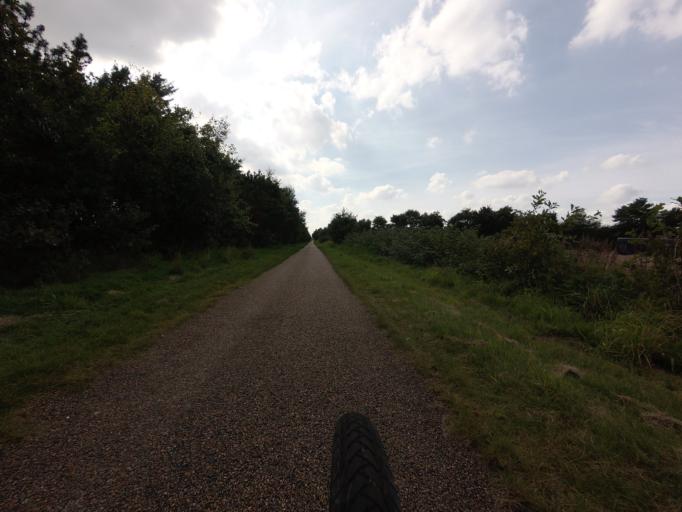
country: DK
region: Central Jutland
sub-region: Herning Kommune
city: Sunds
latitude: 56.2077
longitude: 9.0351
